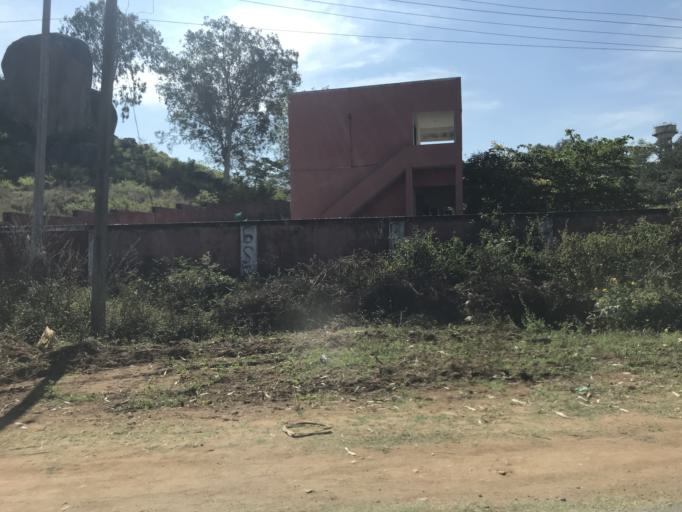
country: IN
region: Karnataka
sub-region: Mysore
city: Heggadadevankote
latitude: 12.1134
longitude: 76.3969
